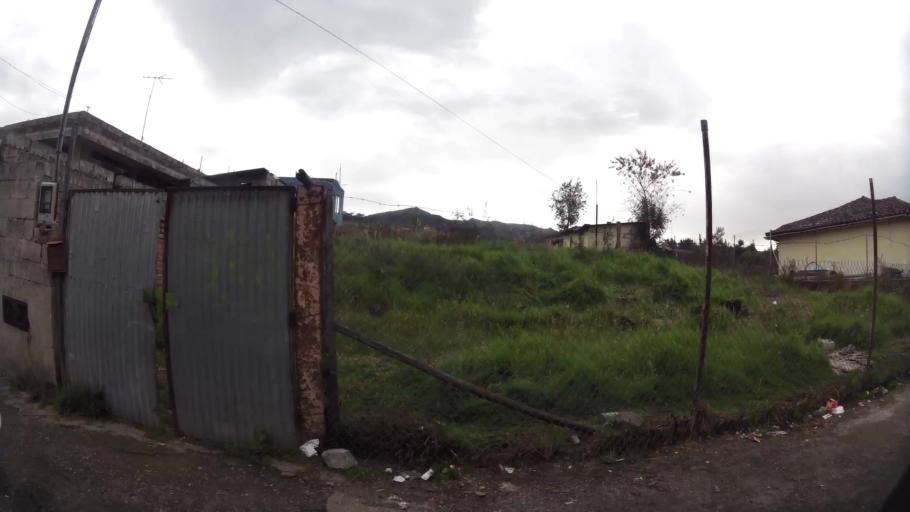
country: EC
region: Pichincha
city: Sangolqui
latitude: -0.3511
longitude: -78.5577
